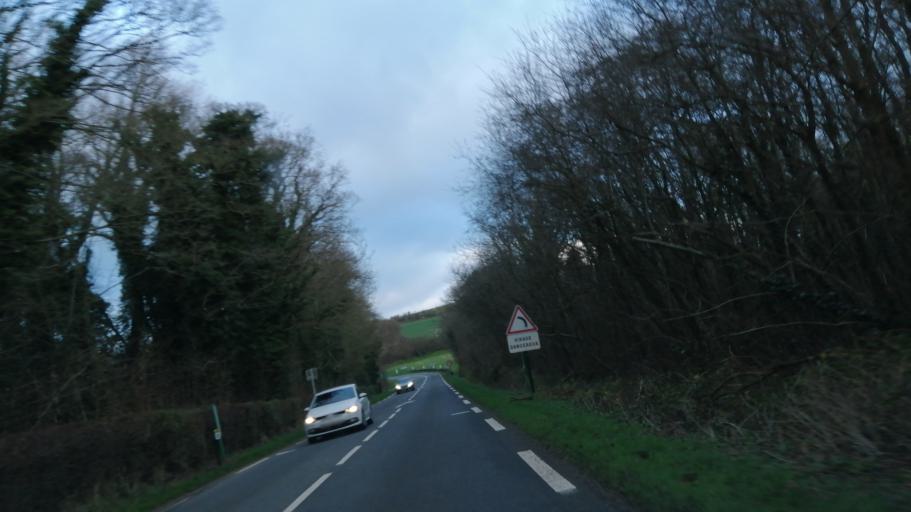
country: FR
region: Nord-Pas-de-Calais
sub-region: Departement du Pas-de-Calais
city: Wissant
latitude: 50.8937
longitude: 1.6846
